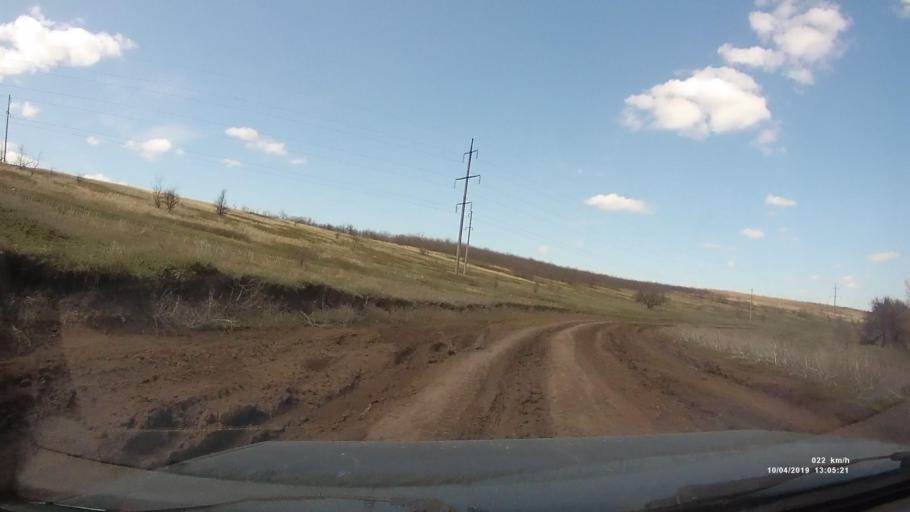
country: RU
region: Rostov
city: Masalovka
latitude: 48.3877
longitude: 40.2330
